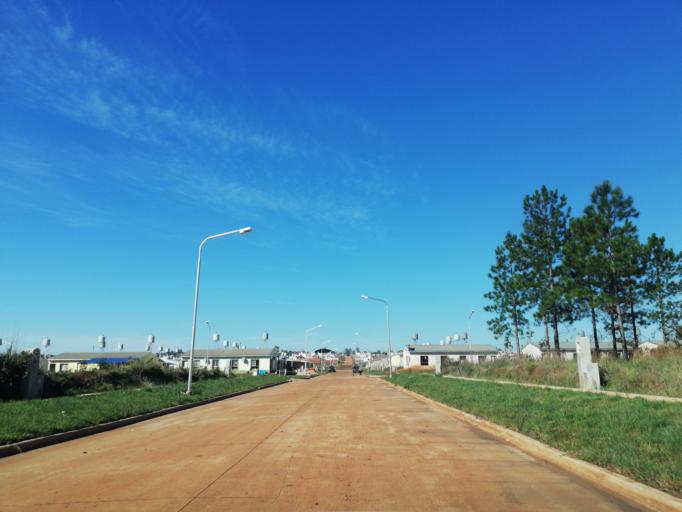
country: AR
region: Misiones
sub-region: Departamento de Capital
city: Posadas
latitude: -27.4053
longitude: -55.9914
